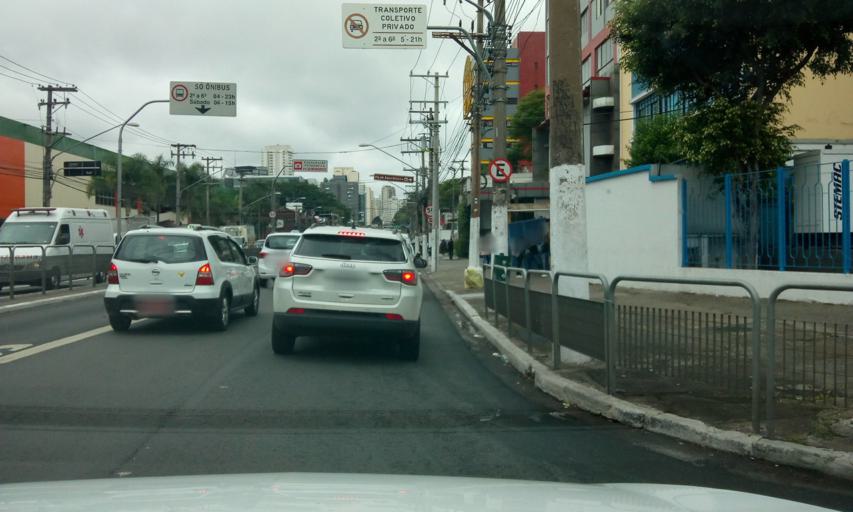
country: BR
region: Sao Paulo
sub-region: Sao Paulo
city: Sao Paulo
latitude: -23.5271
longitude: -46.6726
